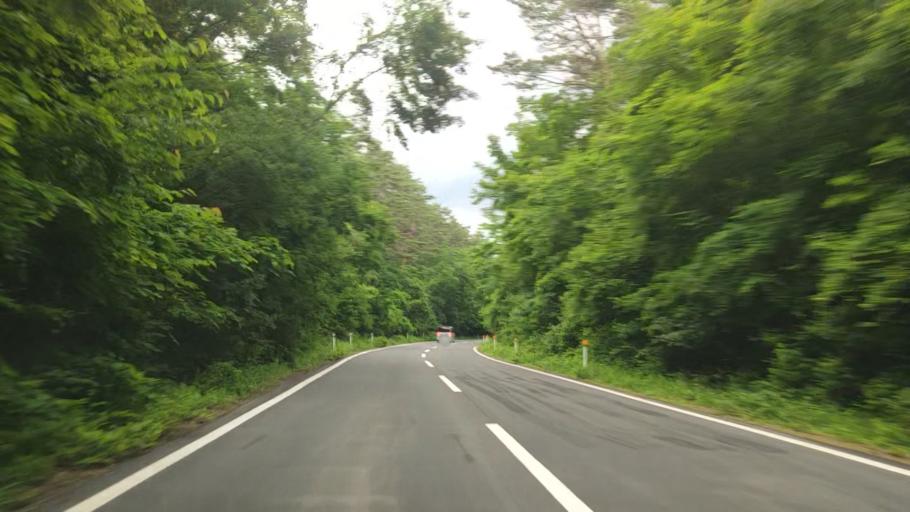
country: JP
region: Yamanashi
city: Fujikawaguchiko
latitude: 35.4700
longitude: 138.7629
